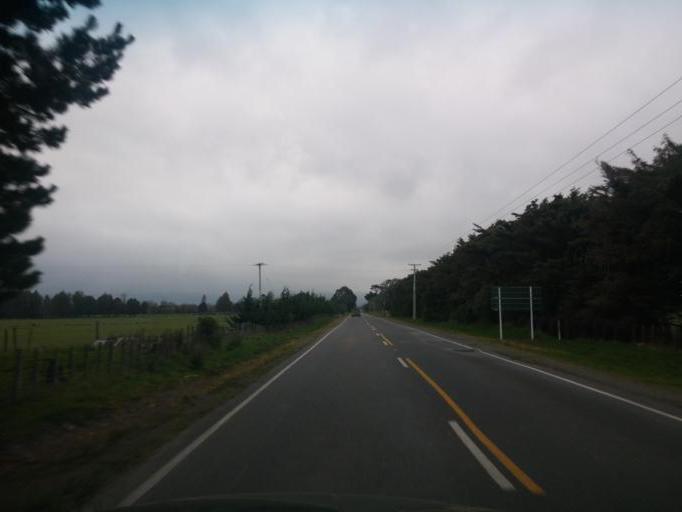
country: NZ
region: Wellington
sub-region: South Wairarapa District
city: Waipawa
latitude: -41.1490
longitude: 175.3668
